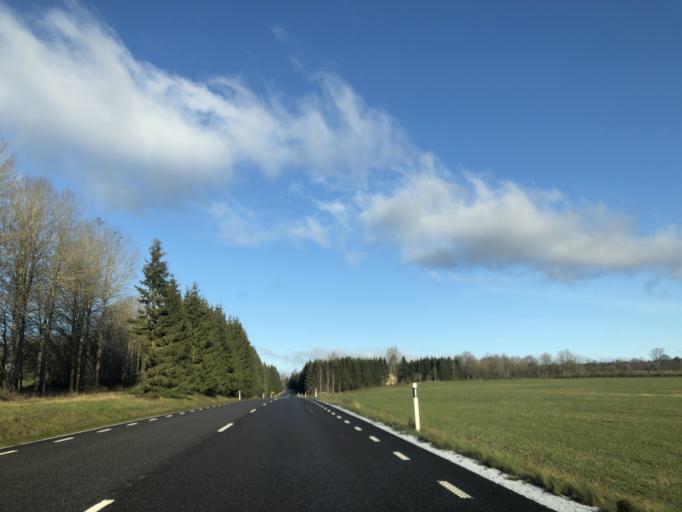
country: SE
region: Vaestra Goetaland
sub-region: Tranemo Kommun
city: Limmared
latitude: 57.6384
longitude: 13.4448
